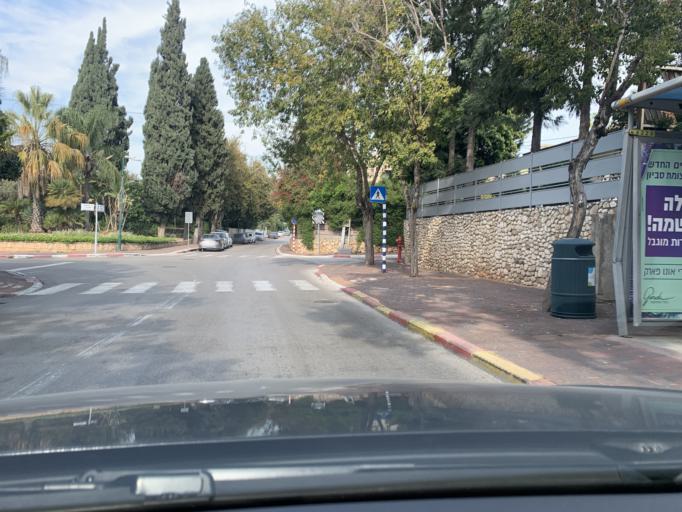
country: IL
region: Central District
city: Ganne Tiqwa
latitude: 32.0605
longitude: 34.8578
